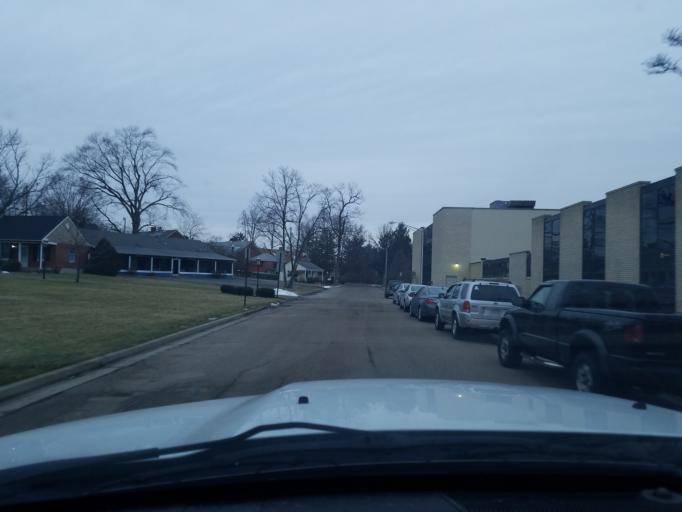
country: US
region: Ohio
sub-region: Montgomery County
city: Oakwood
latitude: 39.7171
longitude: -84.1599
